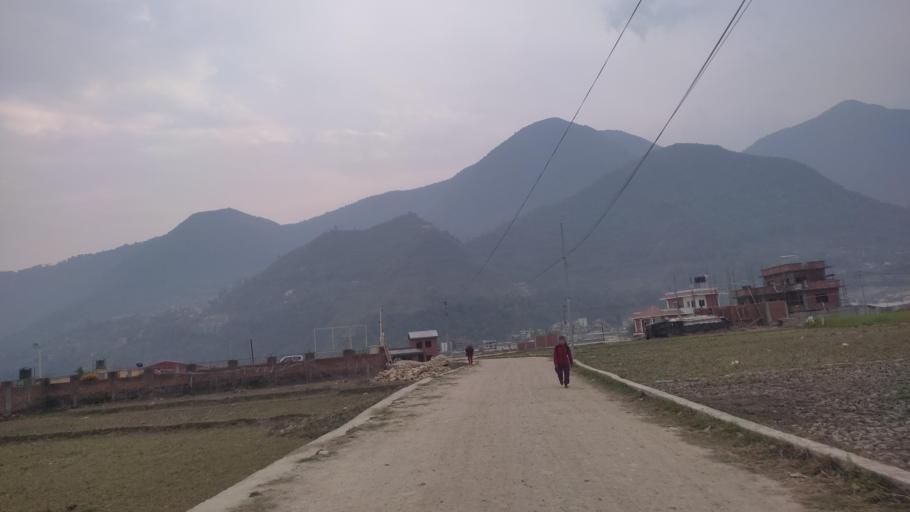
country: NP
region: Central Region
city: Kirtipur
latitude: 27.6632
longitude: 85.2758
